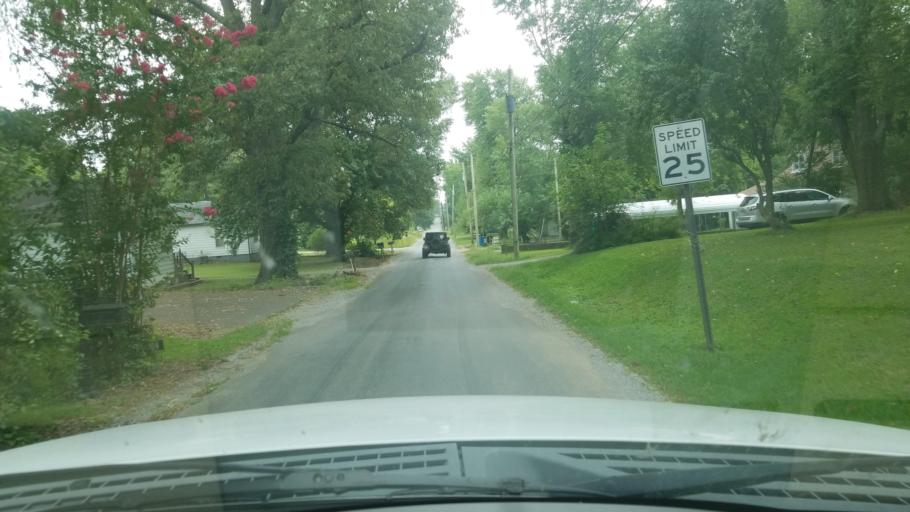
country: US
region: Illinois
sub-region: Saline County
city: Eldorado
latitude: 37.8219
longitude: -88.4477
